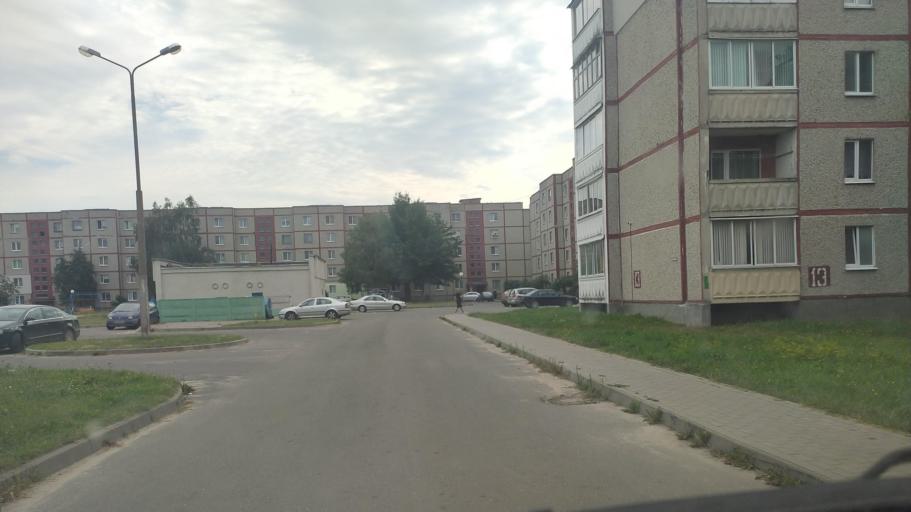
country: BY
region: Brest
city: Byaroza
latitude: 52.5389
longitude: 24.9722
